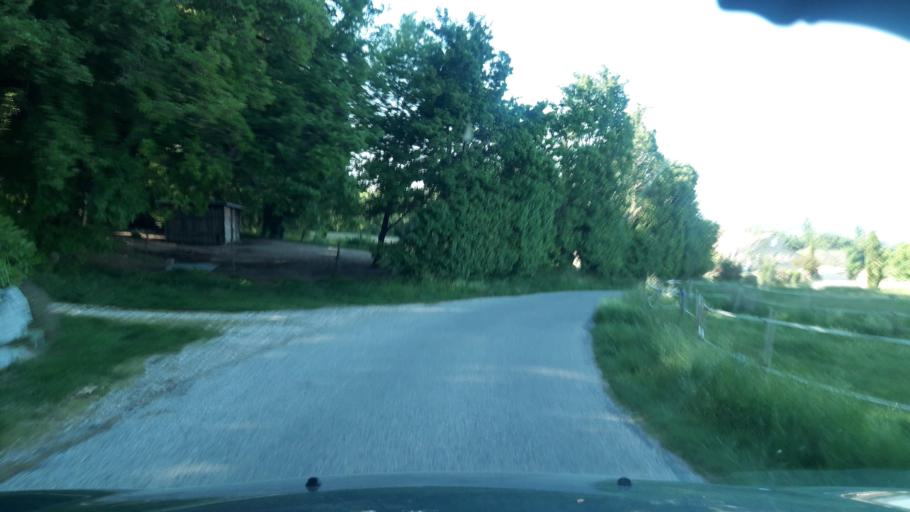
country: FR
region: Rhone-Alpes
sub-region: Departement de la Drome
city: Grane
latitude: 44.7242
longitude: 4.8945
